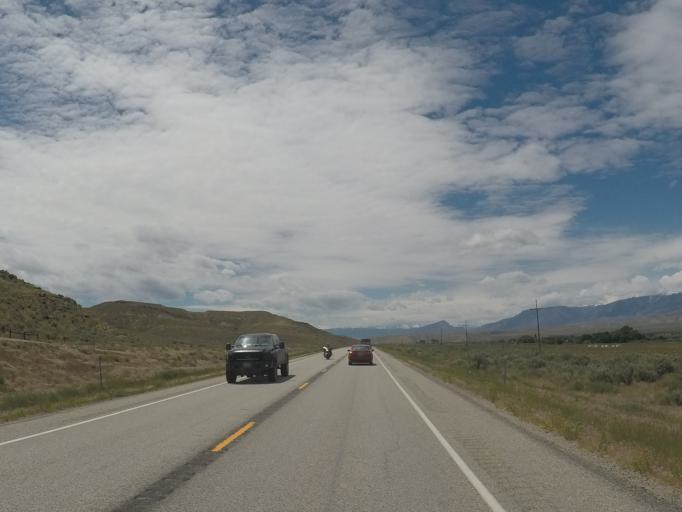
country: US
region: Montana
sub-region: Carbon County
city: Red Lodge
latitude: 45.0600
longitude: -109.0414
